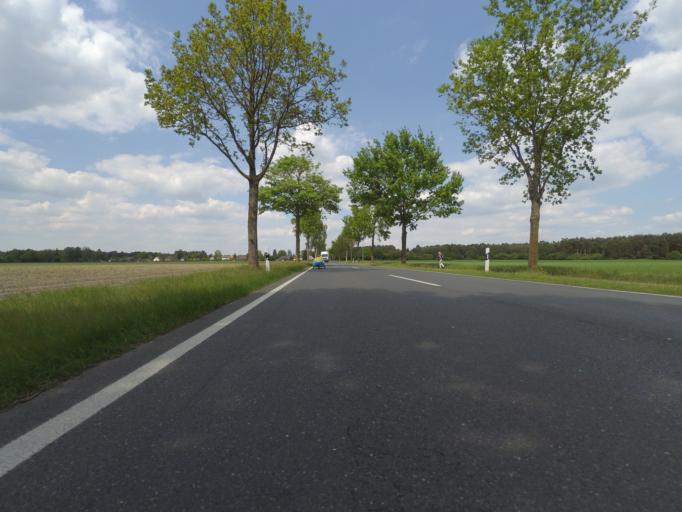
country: DE
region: Lower Saxony
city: Winsen
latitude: 52.6465
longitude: 9.9330
